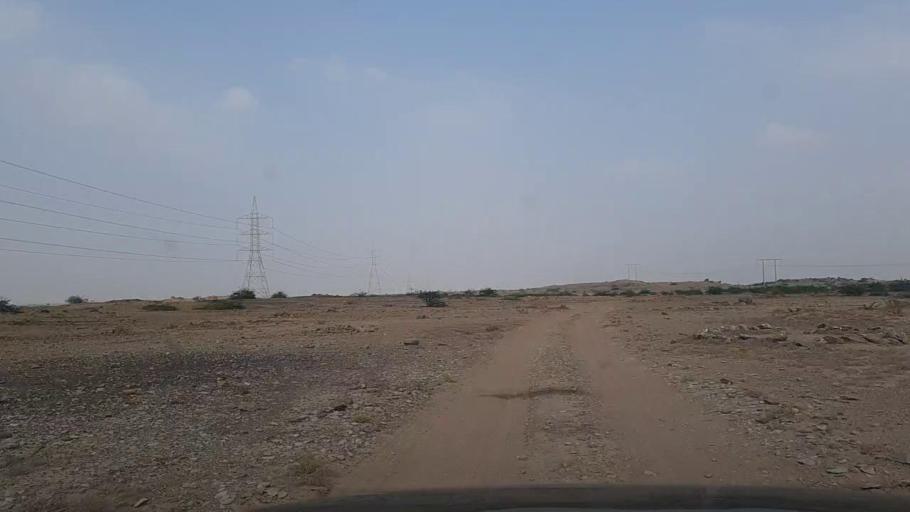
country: PK
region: Sindh
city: Thatta
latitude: 24.8864
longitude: 67.8379
